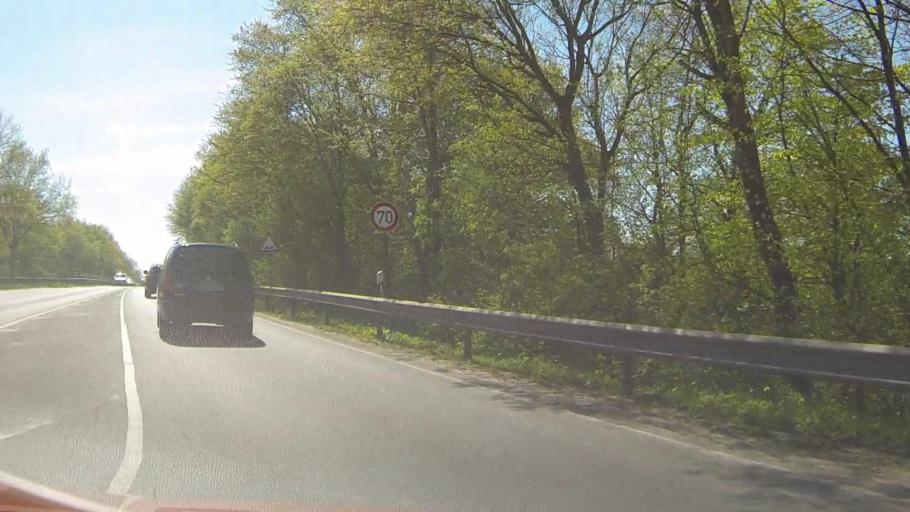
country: DE
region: Schleswig-Holstein
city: Ellerhoop
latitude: 53.7176
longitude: 9.7570
